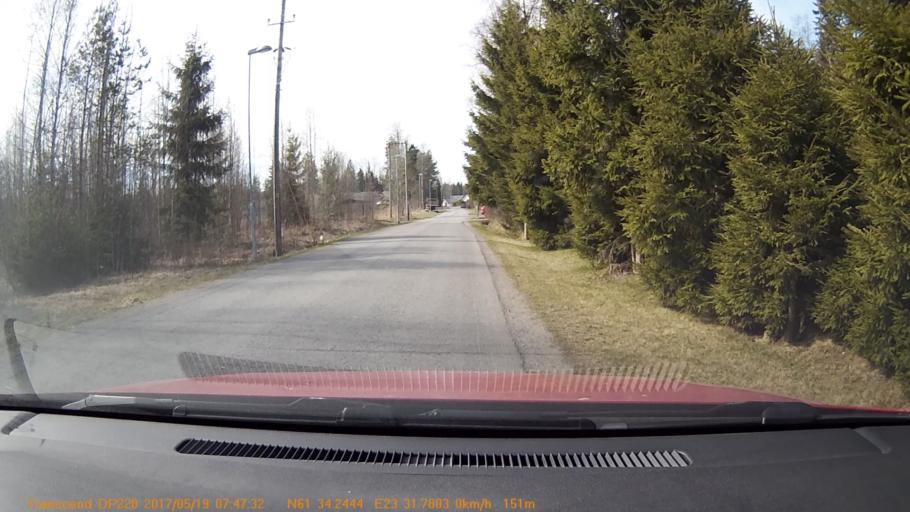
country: FI
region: Pirkanmaa
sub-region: Tampere
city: Yloejaervi
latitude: 61.5707
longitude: 23.5297
